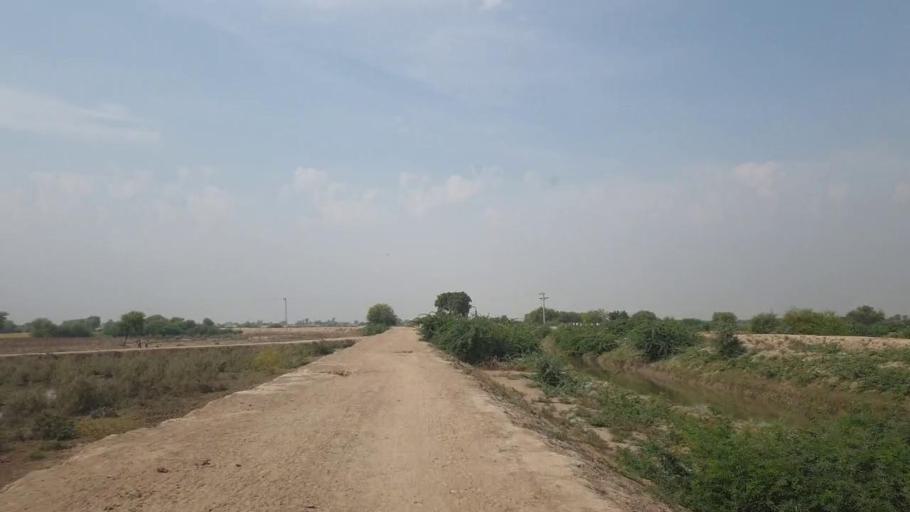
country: PK
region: Sindh
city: Rajo Khanani
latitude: 24.9670
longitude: 69.0111
